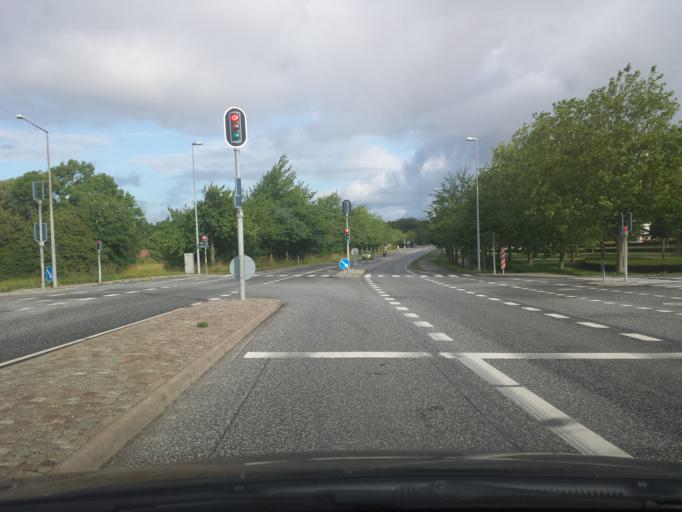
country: DK
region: South Denmark
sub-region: Sonderborg Kommune
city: Guderup
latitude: 55.0333
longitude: 9.8173
